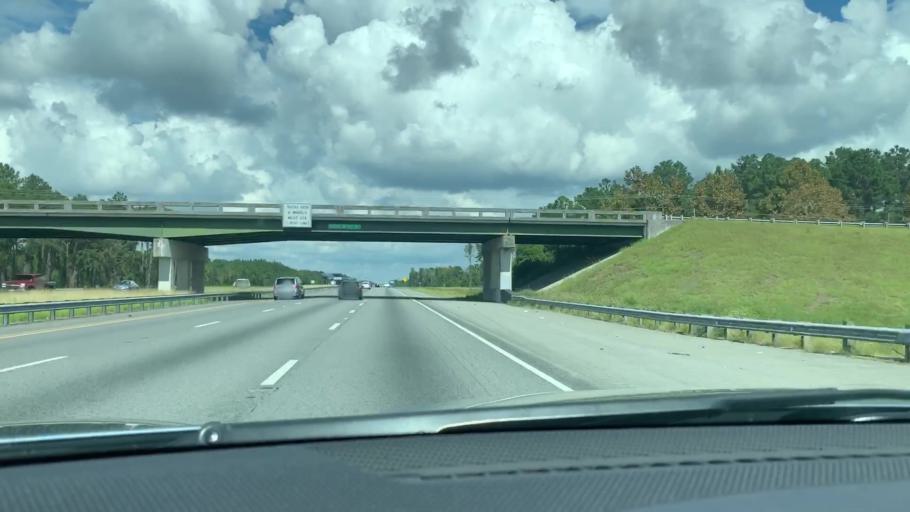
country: US
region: Georgia
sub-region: Glynn County
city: Brunswick
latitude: 31.1014
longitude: -81.5980
